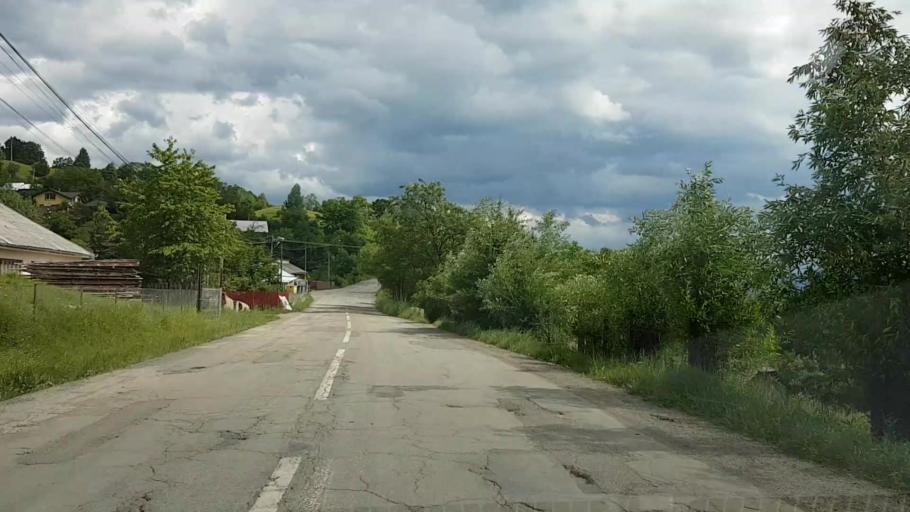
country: RO
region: Neamt
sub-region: Comuna Hangu
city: Hangu
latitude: 47.0430
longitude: 26.0548
